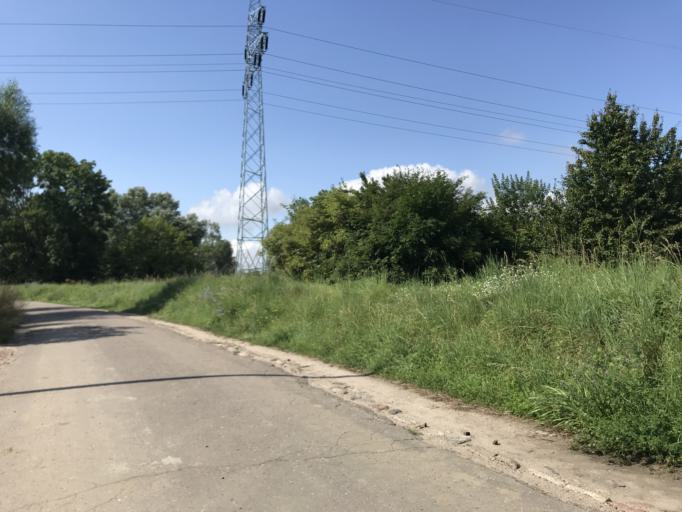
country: PL
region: Pomeranian Voivodeship
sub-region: Gdansk
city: Gdansk
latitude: 54.3295
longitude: 18.6565
